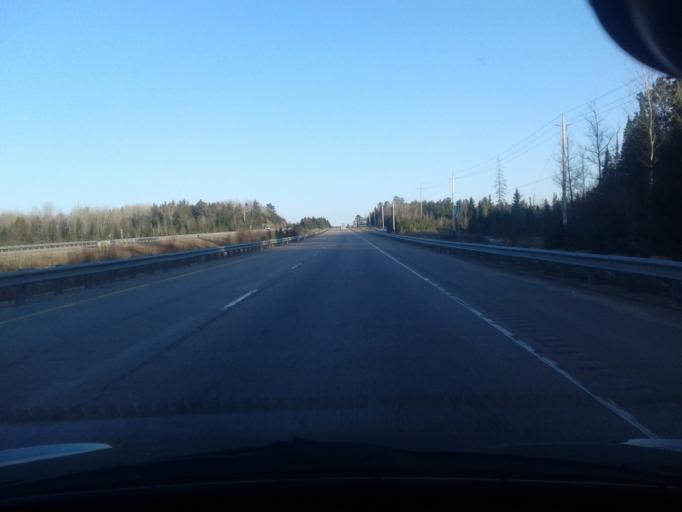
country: CA
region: Ontario
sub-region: Nipissing District
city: North Bay
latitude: 46.2523
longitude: -79.3745
